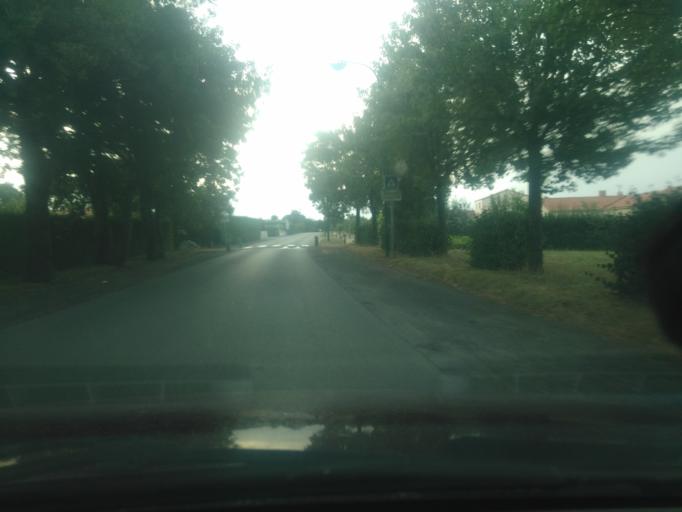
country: FR
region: Pays de la Loire
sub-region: Departement de la Vendee
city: Vendrennes
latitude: 46.7986
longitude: -1.1388
